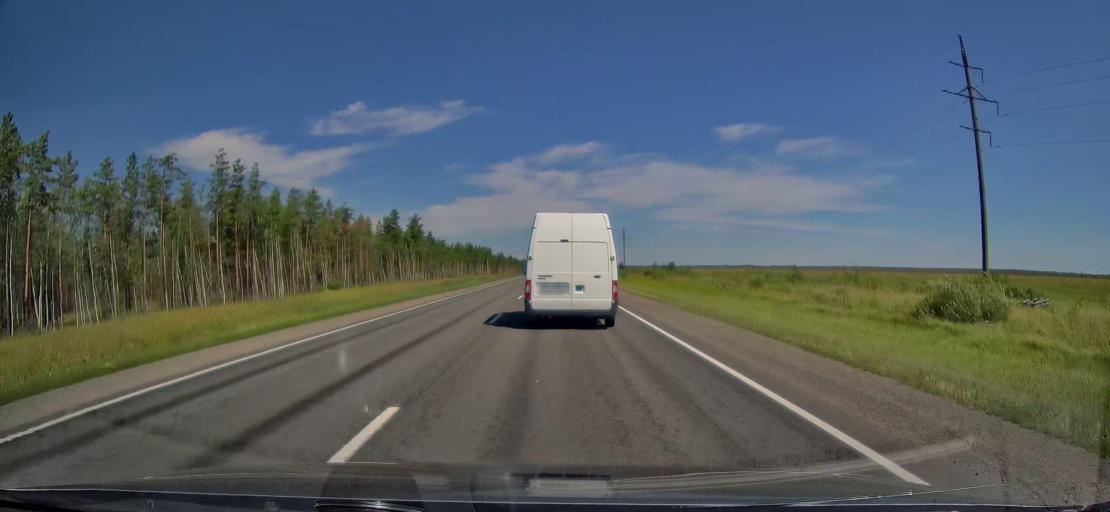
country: RU
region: Vologda
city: Khokhlovo
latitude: 58.9778
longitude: 37.3239
